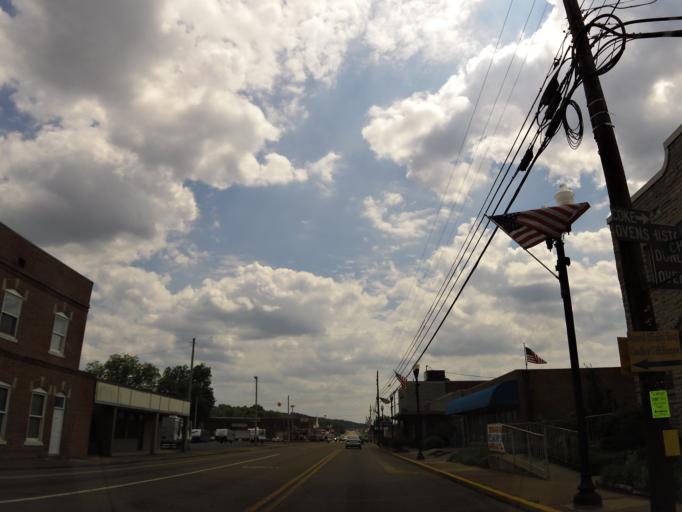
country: US
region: Tennessee
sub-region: Sequatchie County
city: Dunlap
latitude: 35.3716
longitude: -85.3905
